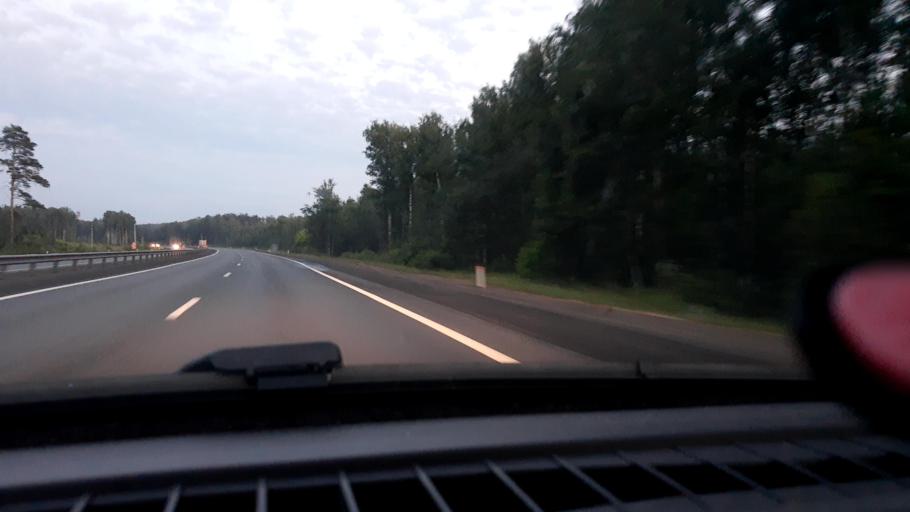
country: RU
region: Nizjnij Novgorod
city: Gorbatovka
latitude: 56.2536
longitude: 43.7113
